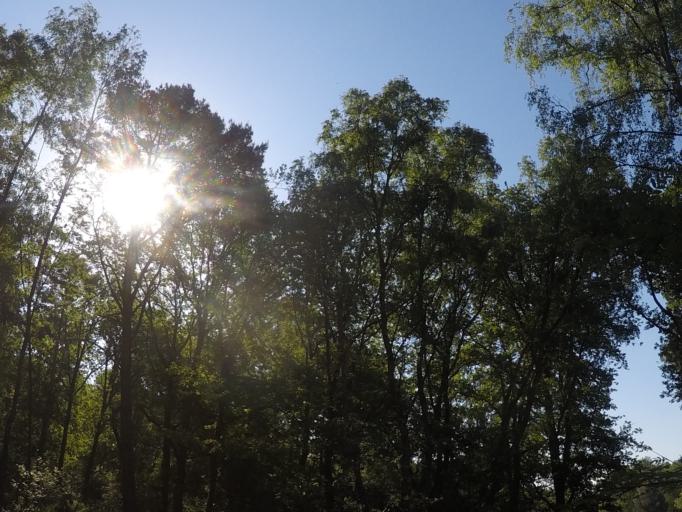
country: NL
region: Gelderland
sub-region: Gemeente Montferland
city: s-Heerenberg
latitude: 51.8819
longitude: 6.1924
